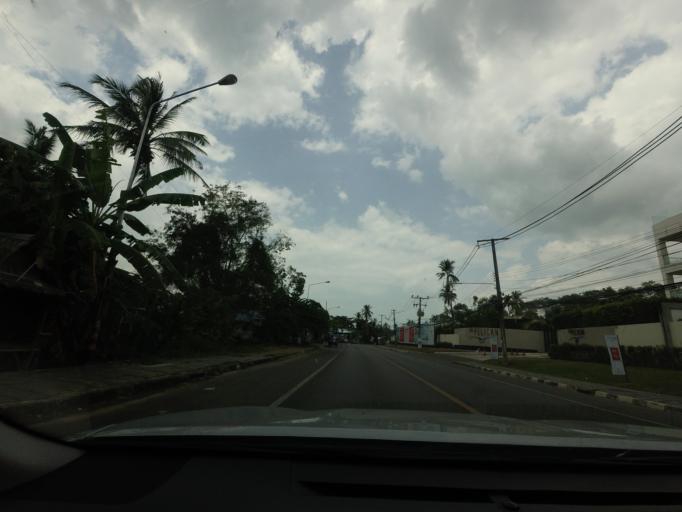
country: TH
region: Phangnga
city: Ban Ao Nang
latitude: 8.0578
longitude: 98.7491
